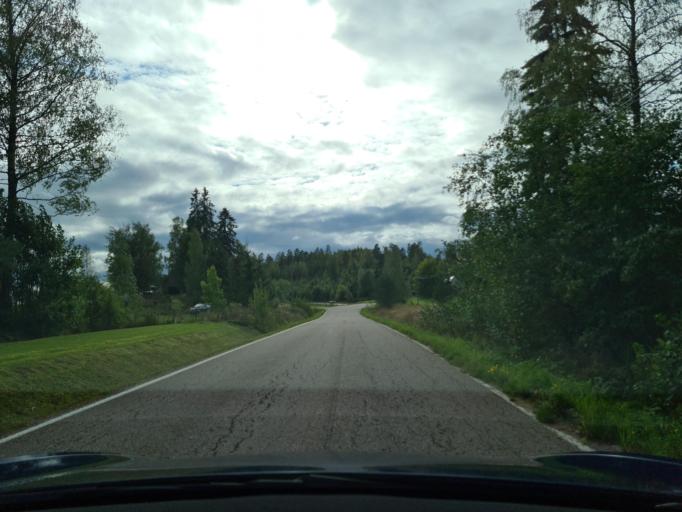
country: FI
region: Uusimaa
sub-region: Helsinki
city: Vihti
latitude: 60.4559
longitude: 24.4069
